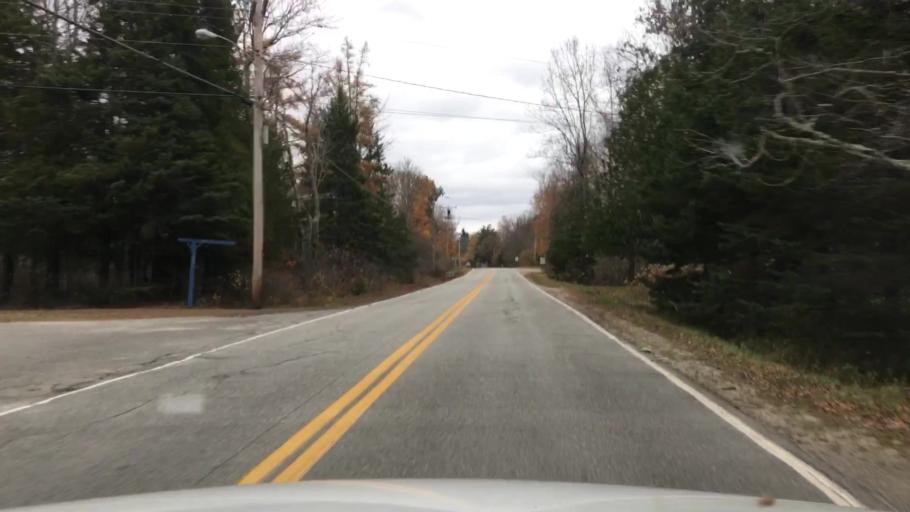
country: US
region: Maine
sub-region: Hancock County
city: Sedgwick
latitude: 44.2679
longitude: -68.5677
